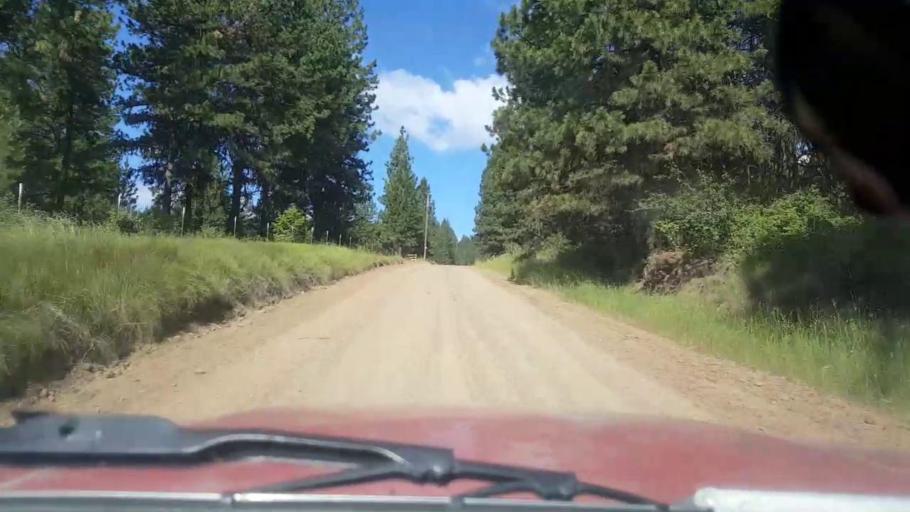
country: US
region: Washington
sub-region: Garfield County
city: Pomeroy
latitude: 46.0370
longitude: -117.4379
